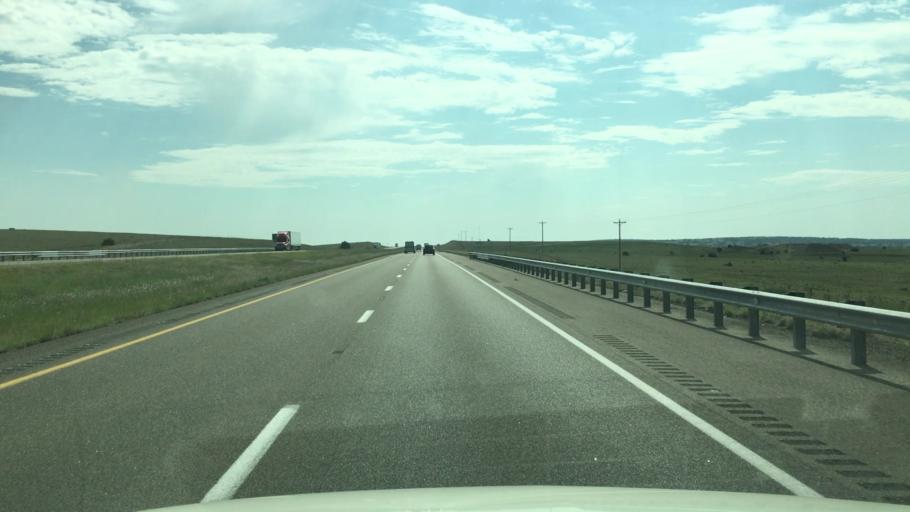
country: US
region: New Mexico
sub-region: Guadalupe County
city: Santa Rosa
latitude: 34.9902
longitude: -105.2717
